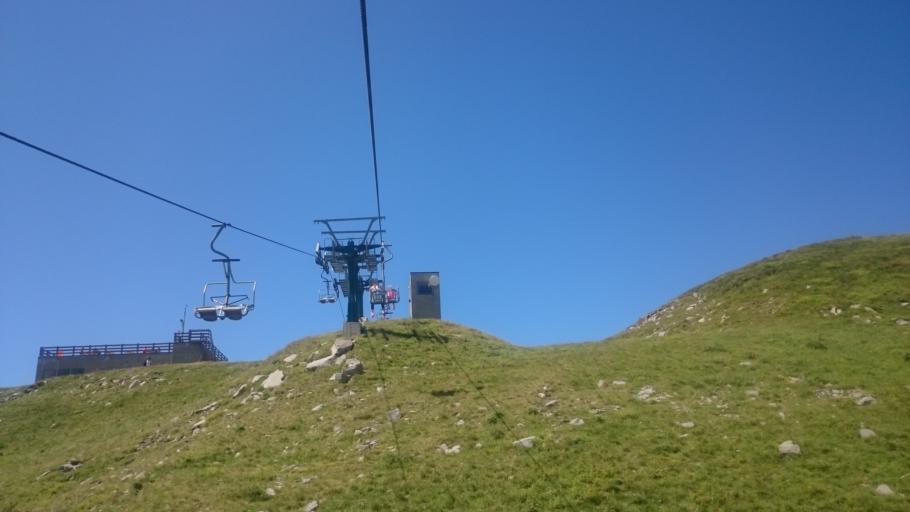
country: IT
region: Emilia-Romagna
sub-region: Provincia di Reggio Emilia
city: Ligonchio
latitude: 44.2827
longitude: 10.4021
